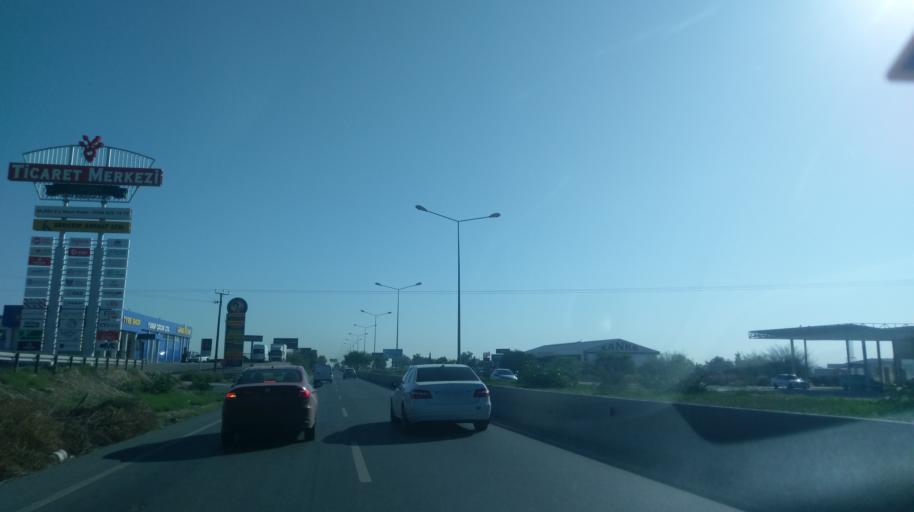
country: CY
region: Lefkosia
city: Nicosia
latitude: 35.2148
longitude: 33.4359
